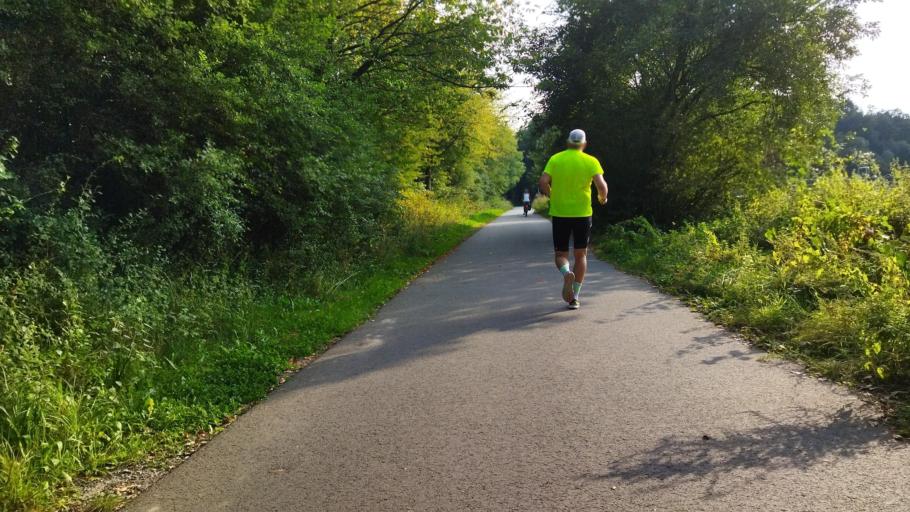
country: DE
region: Lower Saxony
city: Osnabrueck
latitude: 52.2498
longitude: 8.0318
